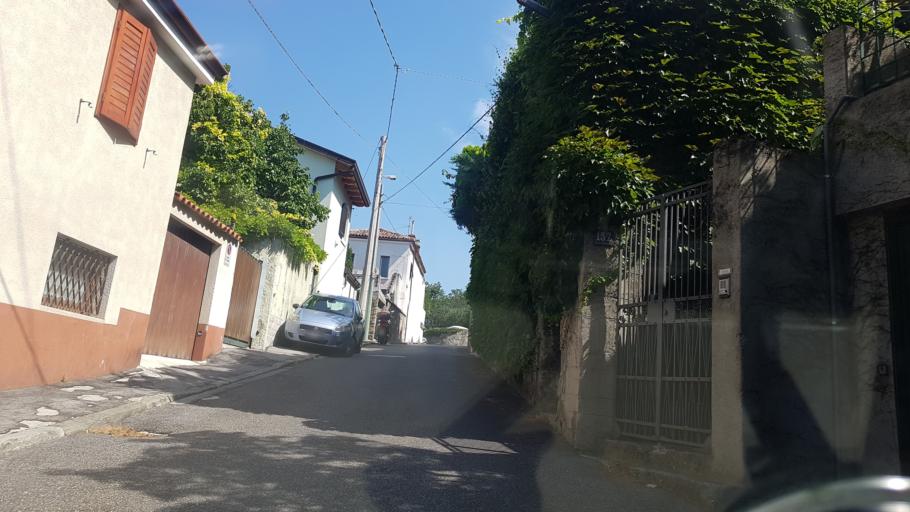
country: IT
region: Friuli Venezia Giulia
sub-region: Provincia di Trieste
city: Trieste
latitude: 45.6621
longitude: 13.7772
